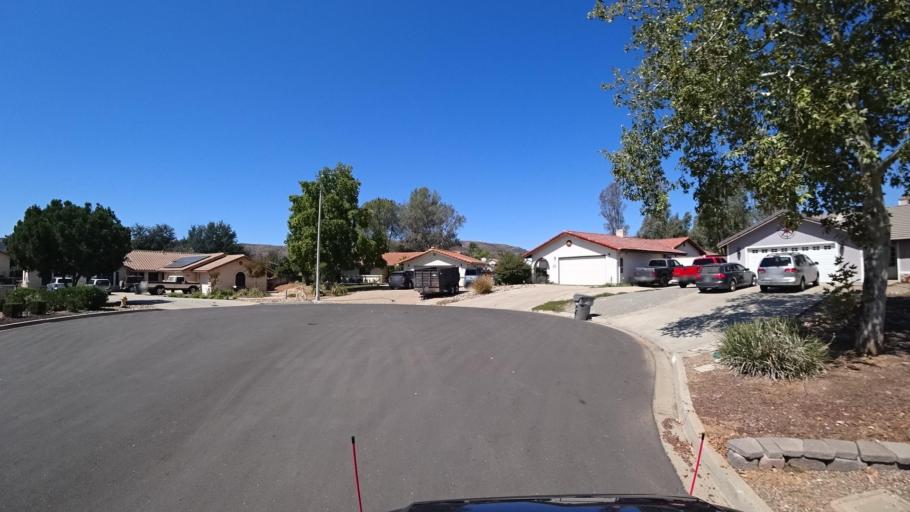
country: US
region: California
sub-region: San Diego County
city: San Diego Country Estates
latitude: 33.0146
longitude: -116.8093
